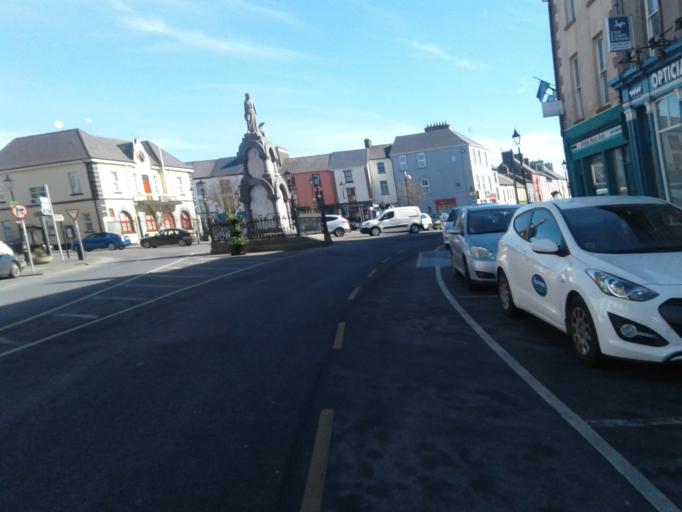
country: IE
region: Munster
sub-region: An Clar
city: Kilrush
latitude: 52.6376
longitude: -9.4851
